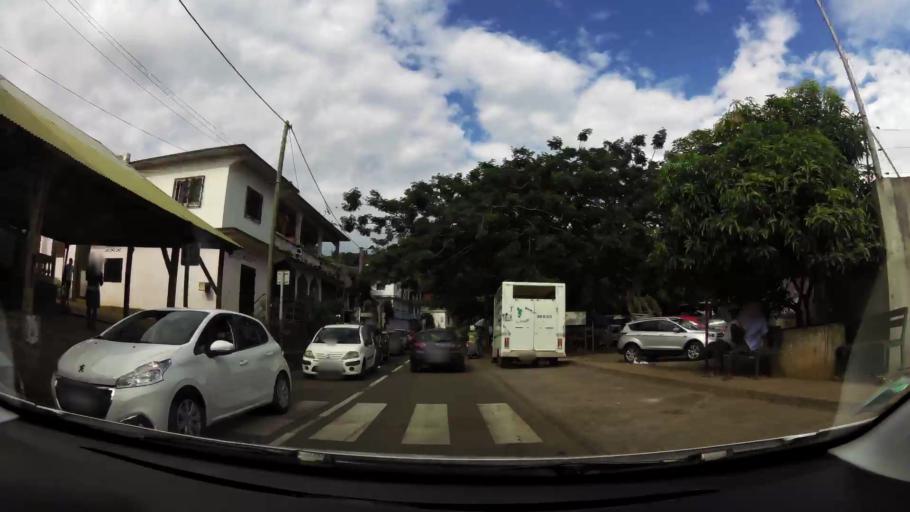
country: YT
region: Chiconi
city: Chiconi
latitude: -12.8443
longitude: 45.1160
